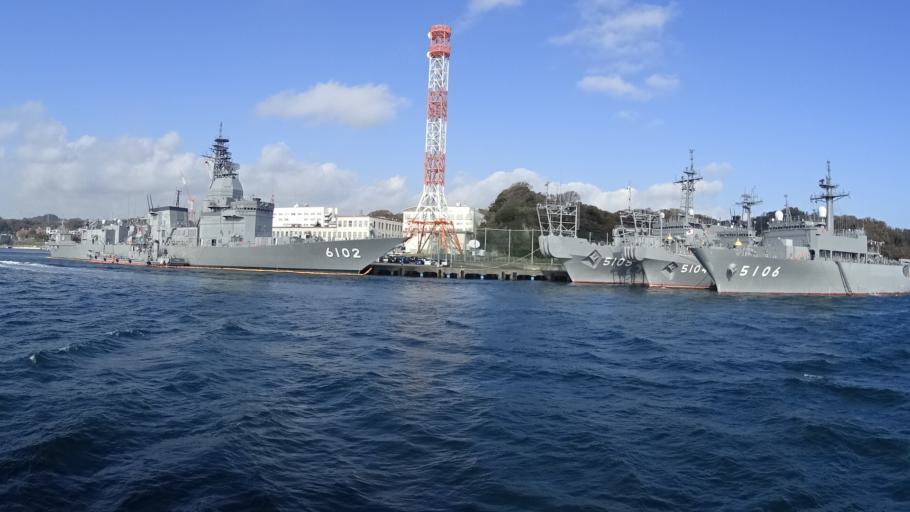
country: JP
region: Kanagawa
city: Yokosuka
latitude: 35.2997
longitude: 139.6396
